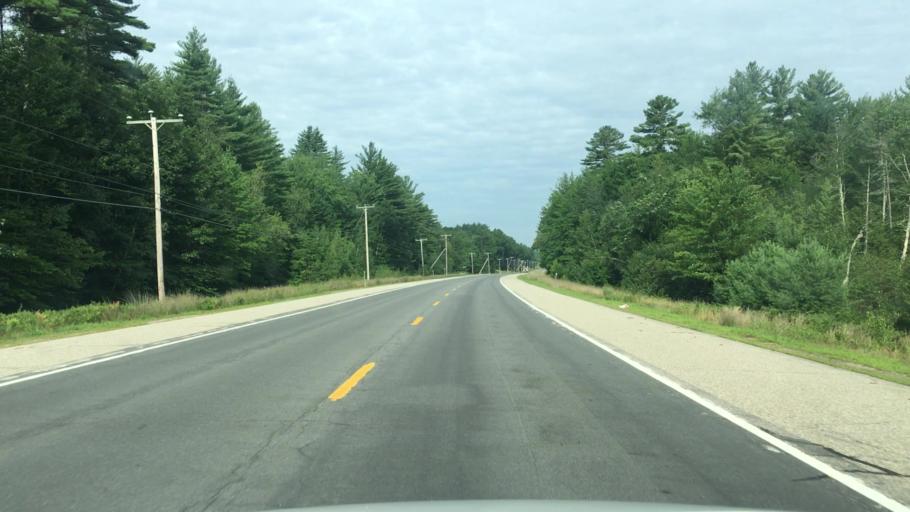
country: US
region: New Hampshire
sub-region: Carroll County
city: Tamworth
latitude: 43.8261
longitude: -71.2498
